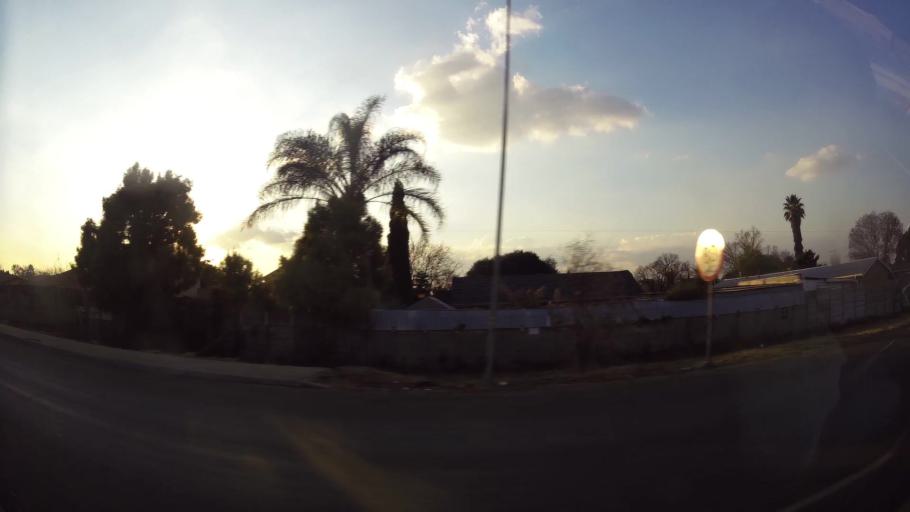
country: ZA
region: Gauteng
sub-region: Ekurhuleni Metropolitan Municipality
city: Boksburg
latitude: -26.2661
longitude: 28.2975
